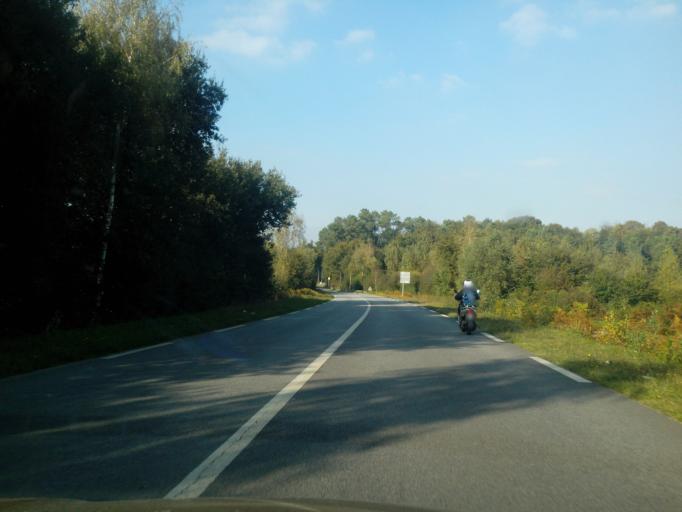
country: FR
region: Brittany
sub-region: Departement du Morbihan
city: Molac
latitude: 47.7190
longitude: -2.4391
